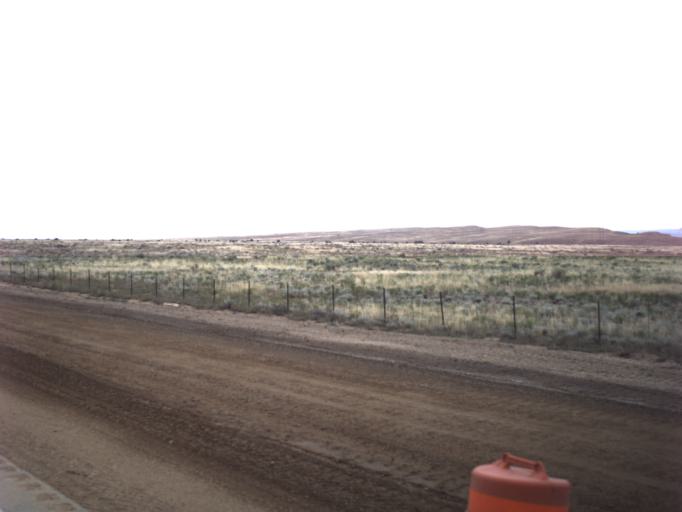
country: US
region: Utah
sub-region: Carbon County
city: East Carbon City
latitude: 39.4367
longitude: -110.4592
